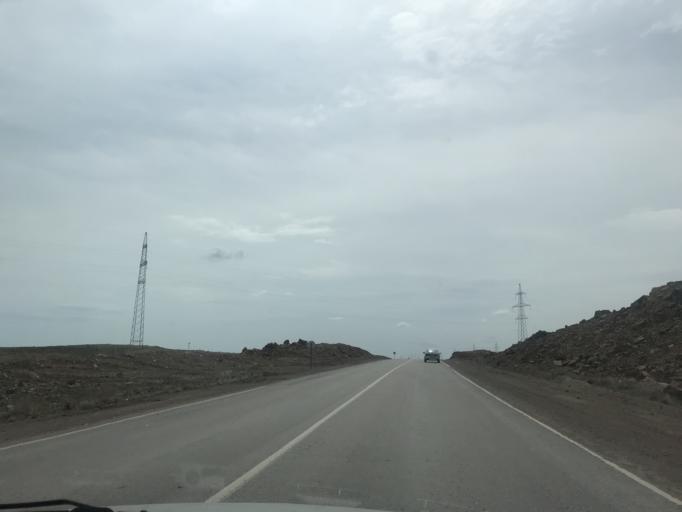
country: KZ
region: Zhambyl
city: Mynaral
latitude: 45.3524
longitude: 73.6858
